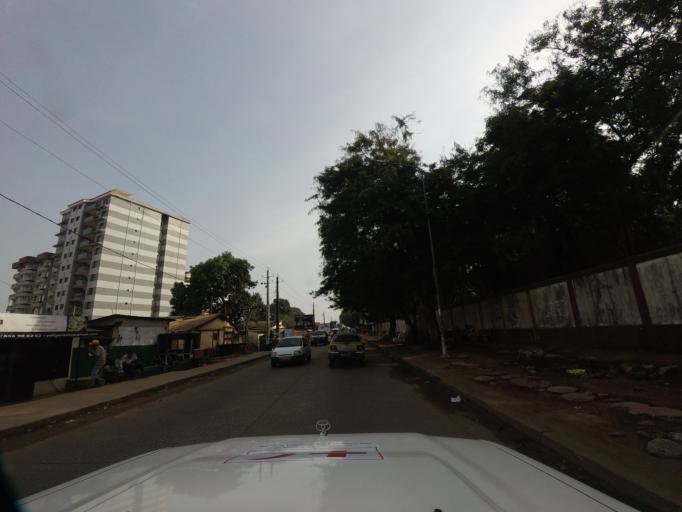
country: GN
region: Conakry
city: Camayenne
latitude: 9.5299
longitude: -13.6875
